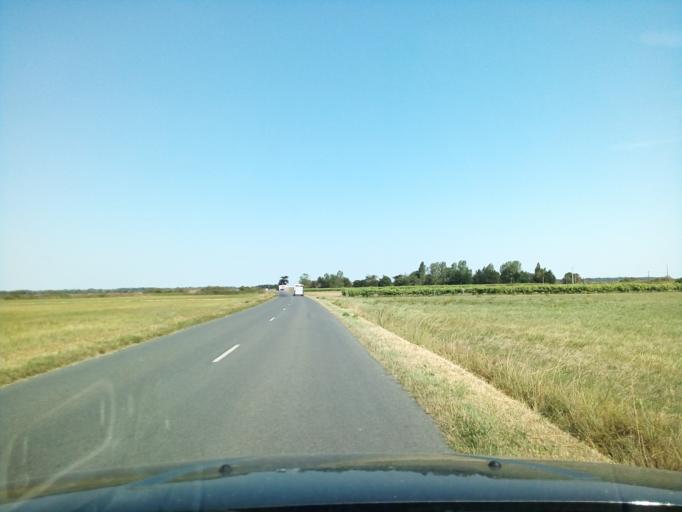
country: FR
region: Poitou-Charentes
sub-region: Departement de la Charente-Maritime
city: Boyard-Ville
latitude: 45.9696
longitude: -1.2844
